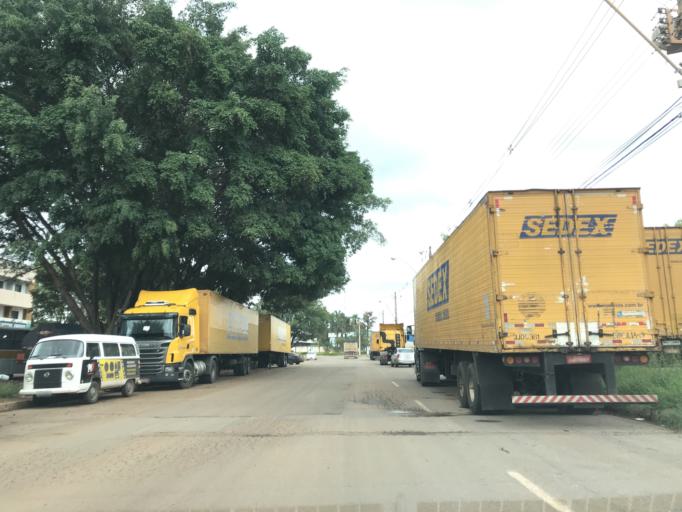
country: BR
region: Federal District
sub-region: Brasilia
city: Brasilia
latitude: -15.7903
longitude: -47.9869
